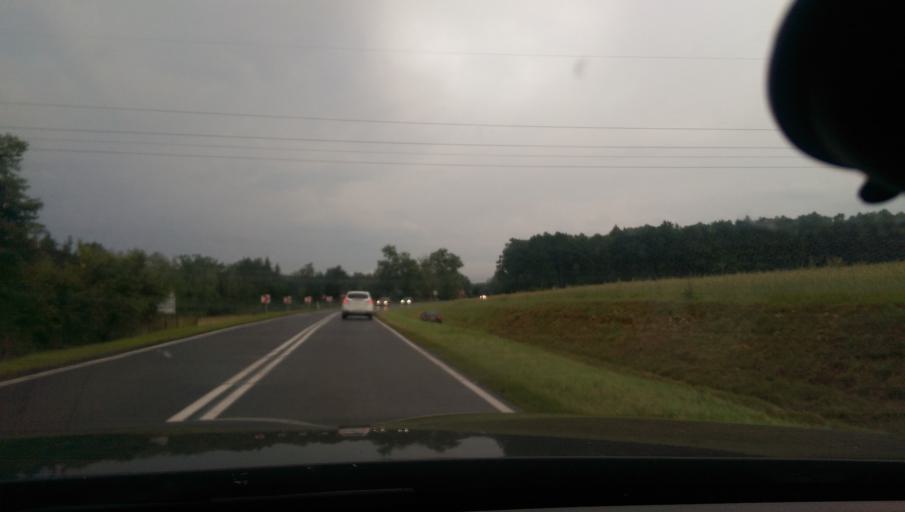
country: PL
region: Warmian-Masurian Voivodeship
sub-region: Powiat szczycienski
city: Szczytno
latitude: 53.5423
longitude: 20.9890
